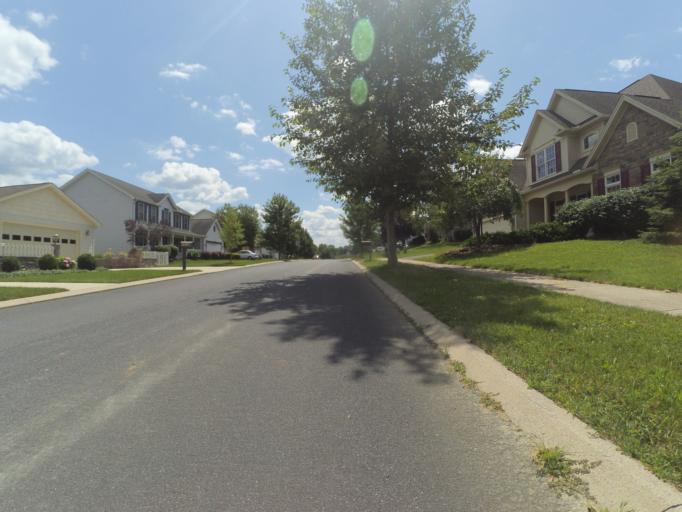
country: US
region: Pennsylvania
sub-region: Centre County
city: Lemont
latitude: 40.8044
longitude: -77.8296
